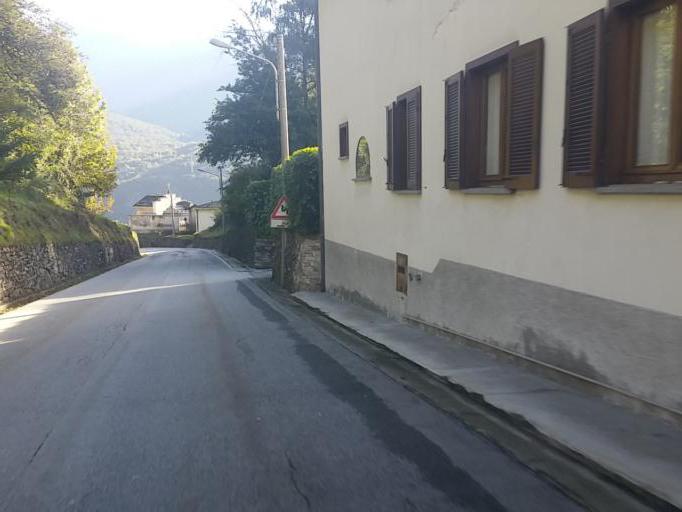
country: IT
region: Piedmont
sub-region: Provincia Verbano-Cusio-Ossola
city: Crevoladossola
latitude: 46.1533
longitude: 8.3002
